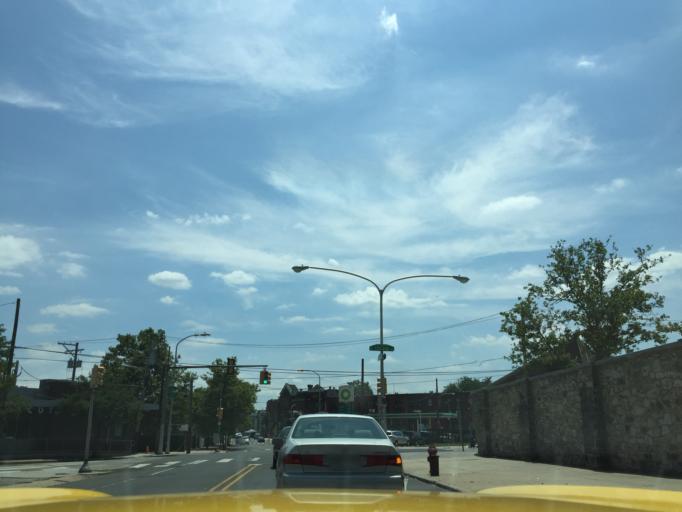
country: US
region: Pennsylvania
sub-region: Philadelphia County
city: Philadelphia
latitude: 39.9739
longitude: -75.1675
